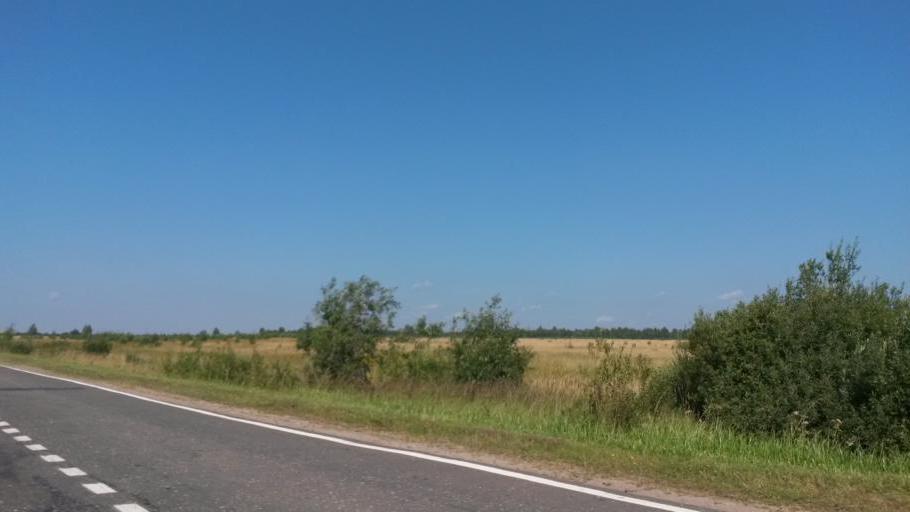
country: RU
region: Jaroslavl
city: Tutayev
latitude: 57.9493
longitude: 39.4587
